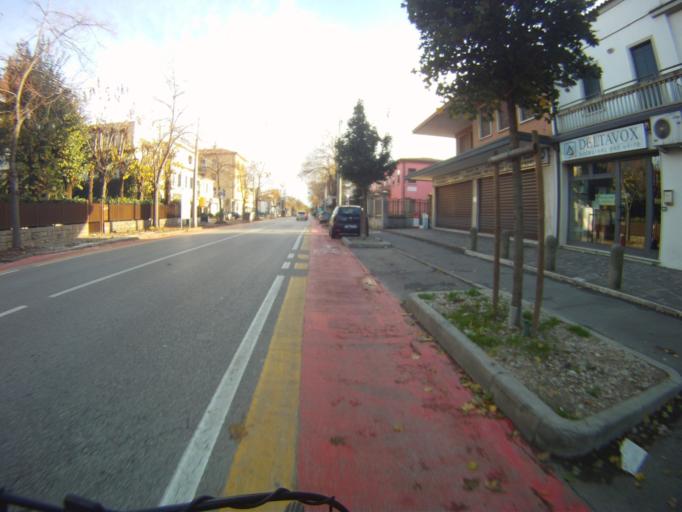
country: IT
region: Veneto
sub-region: Provincia di Padova
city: Padova
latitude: 45.3921
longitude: 11.8919
